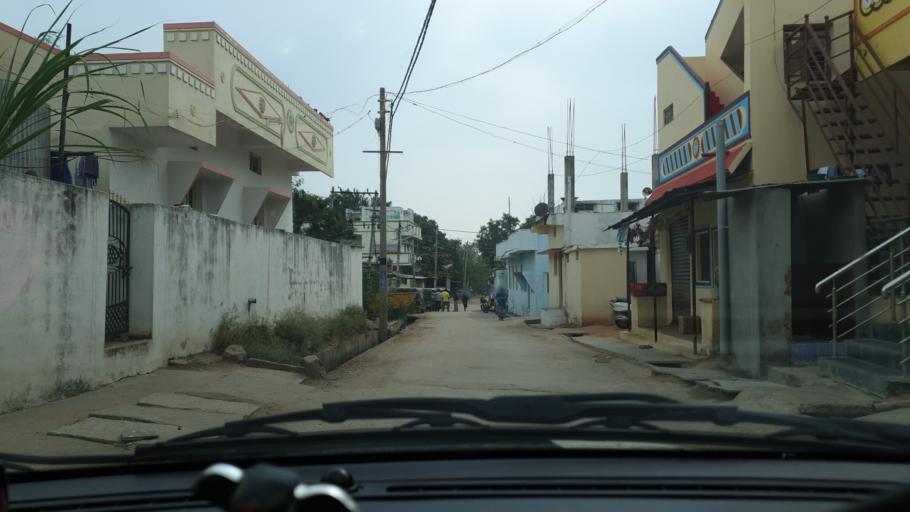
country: IN
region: Karnataka
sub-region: Yadgir
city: Gurmatkal
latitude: 16.8608
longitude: 77.3928
